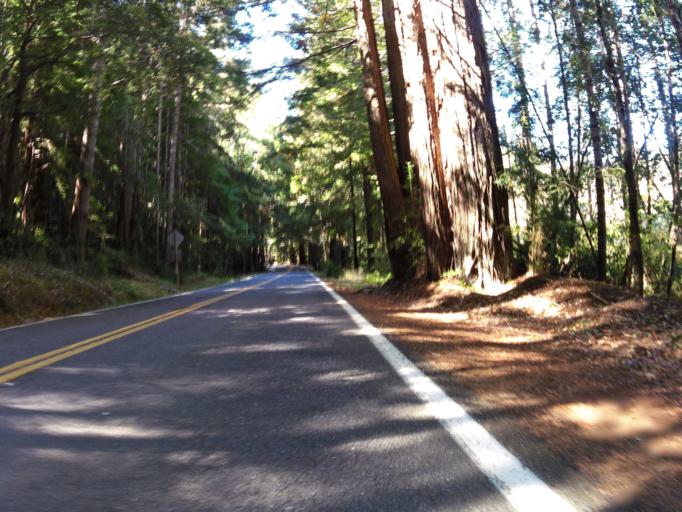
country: US
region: California
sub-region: Humboldt County
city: Redway
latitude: 39.8101
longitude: -123.7917
